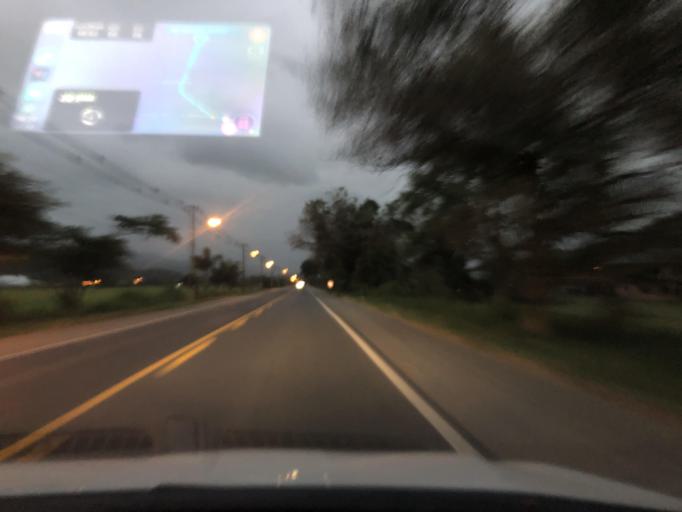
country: BR
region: Santa Catarina
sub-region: Jaragua Do Sul
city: Jaragua do Sul
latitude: -26.6287
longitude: -49.0123
